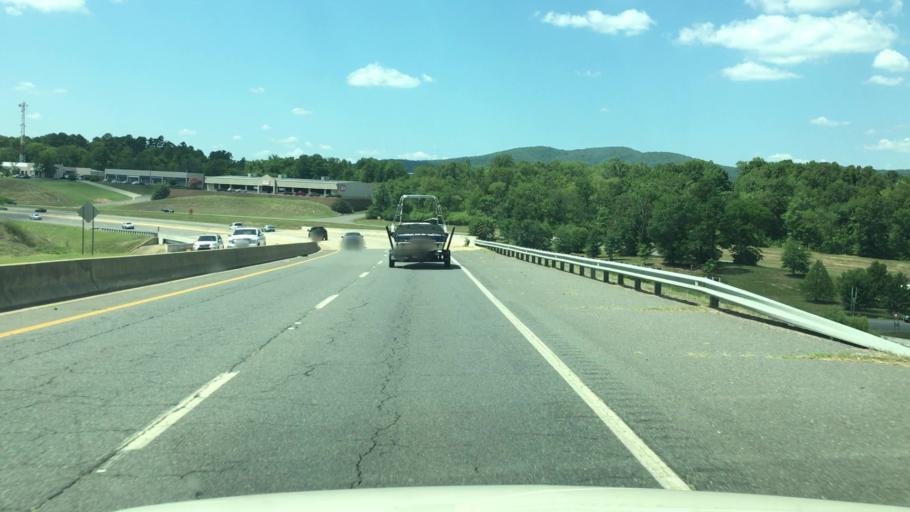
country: US
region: Arkansas
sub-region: Garland County
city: Lake Hamilton
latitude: 34.4691
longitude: -93.0885
